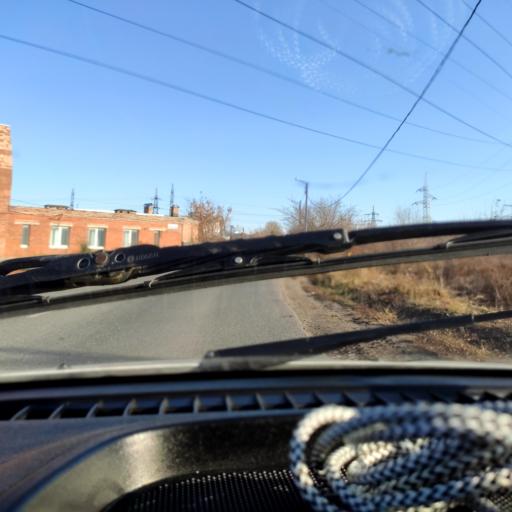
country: RU
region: Samara
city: Zhigulevsk
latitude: 53.5150
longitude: 49.4719
